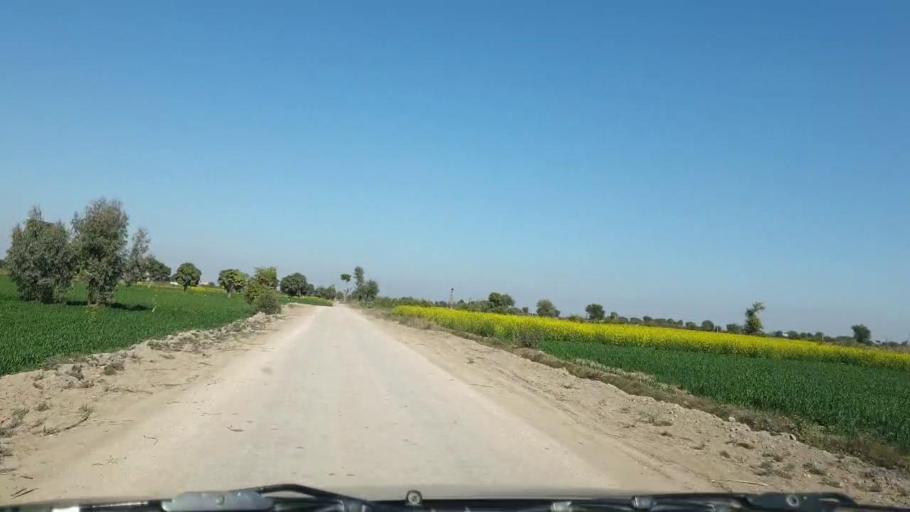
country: PK
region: Sindh
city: Khadro
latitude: 26.1454
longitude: 68.8156
